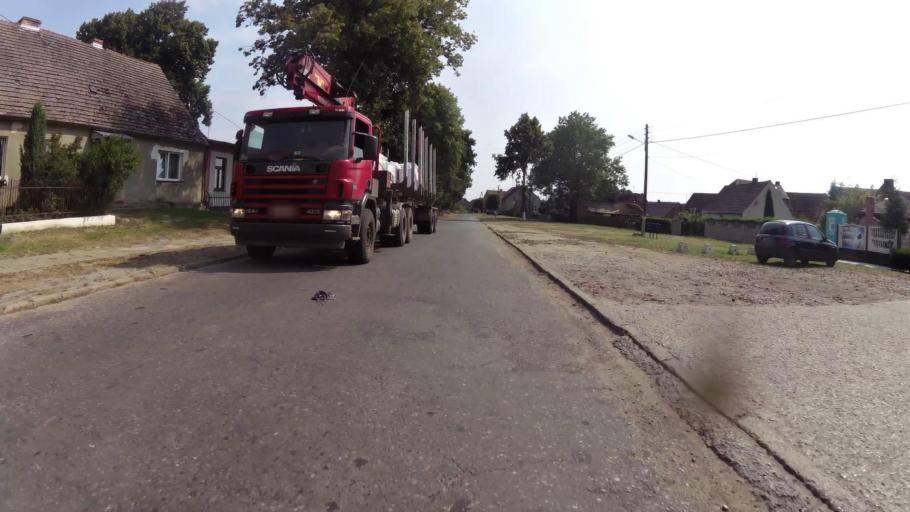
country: PL
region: West Pomeranian Voivodeship
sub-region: Powiat mysliborski
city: Mysliborz
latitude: 52.8460
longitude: 14.7874
